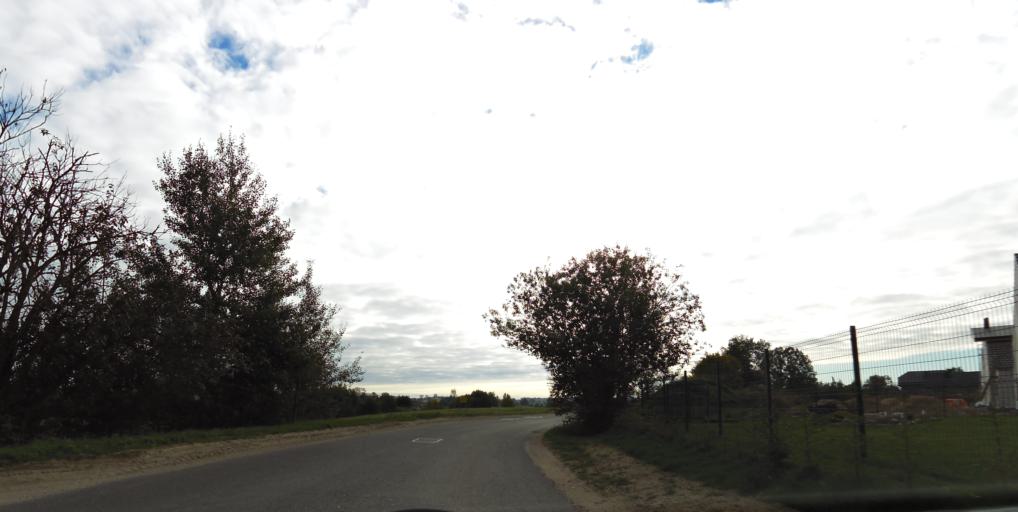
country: LT
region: Vilnius County
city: Pilaite
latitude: 54.7215
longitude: 25.1572
